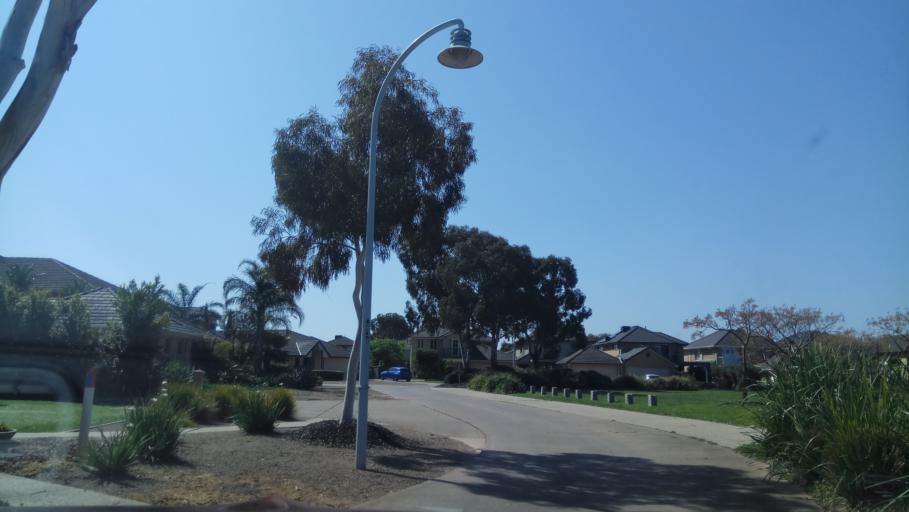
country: AU
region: Victoria
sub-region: Hobsons Bay
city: Altona Meadows
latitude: -37.8861
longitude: 144.7634
